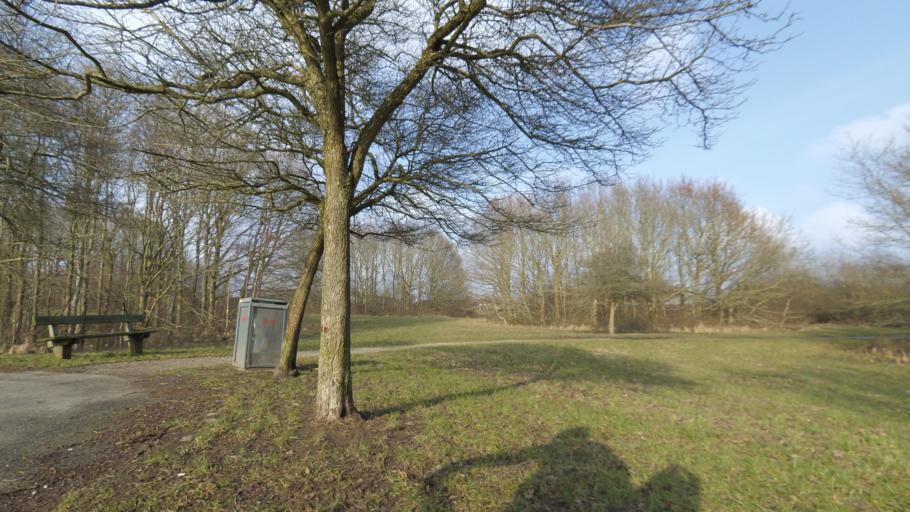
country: DK
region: Central Jutland
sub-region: Arhus Kommune
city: Tranbjerg
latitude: 56.0881
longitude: 10.1442
